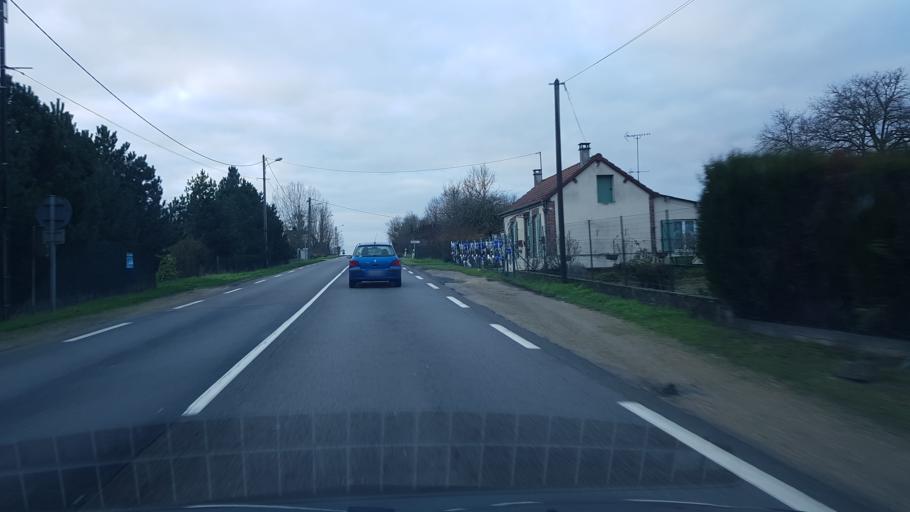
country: FR
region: Champagne-Ardenne
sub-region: Departement de la Marne
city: Esternay
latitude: 48.7132
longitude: 3.4843
